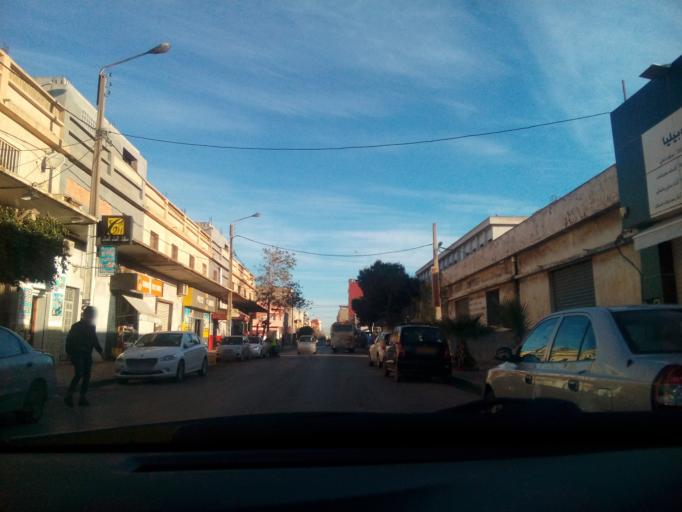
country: DZ
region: Oran
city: Oran
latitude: 35.6812
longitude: -0.6593
